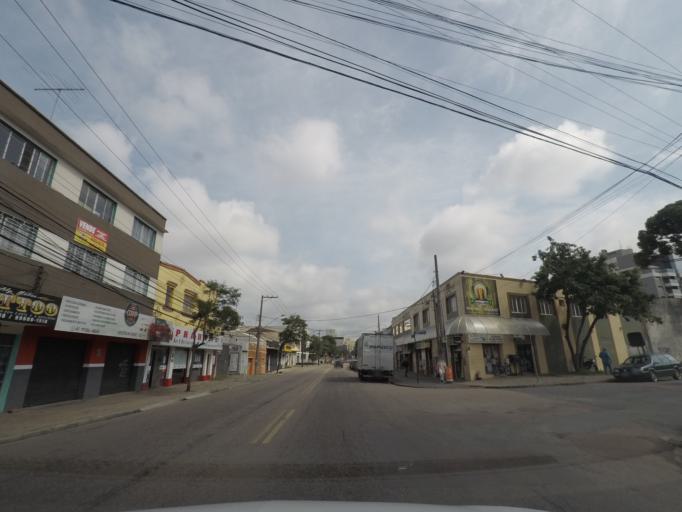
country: BR
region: Parana
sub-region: Curitiba
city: Curitiba
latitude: -25.4753
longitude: -49.2976
